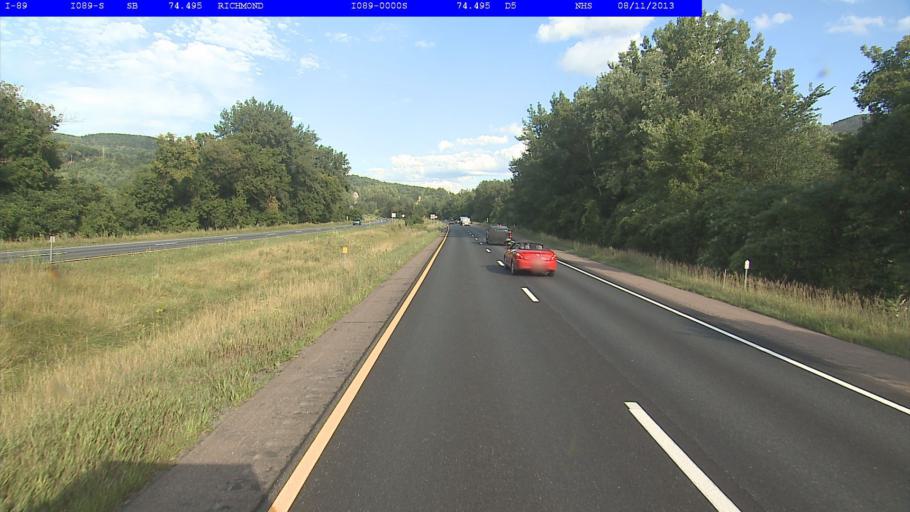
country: US
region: Vermont
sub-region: Chittenden County
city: Jericho
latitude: 44.3905
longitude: -72.9528
